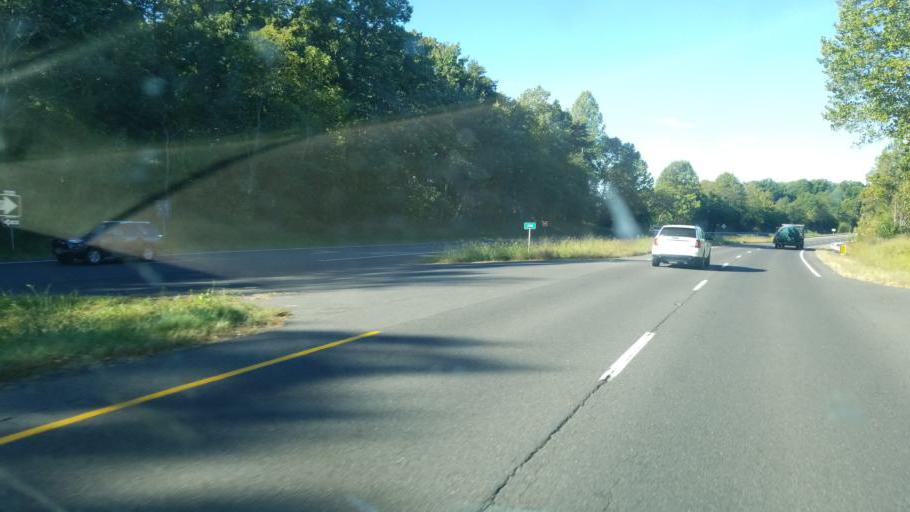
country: US
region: Virginia
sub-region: Madison County
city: Brightwood
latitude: 38.4375
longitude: -78.1398
